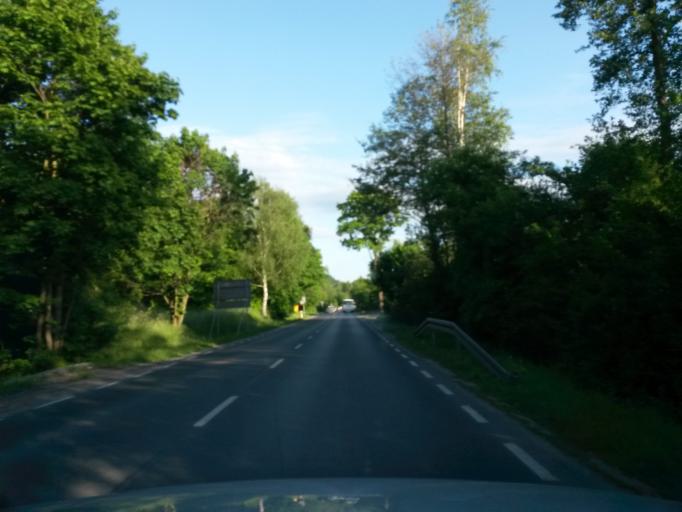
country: PL
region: Lower Silesian Voivodeship
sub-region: Jelenia Gora
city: Jelenia Gora
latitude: 50.8866
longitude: 15.7558
